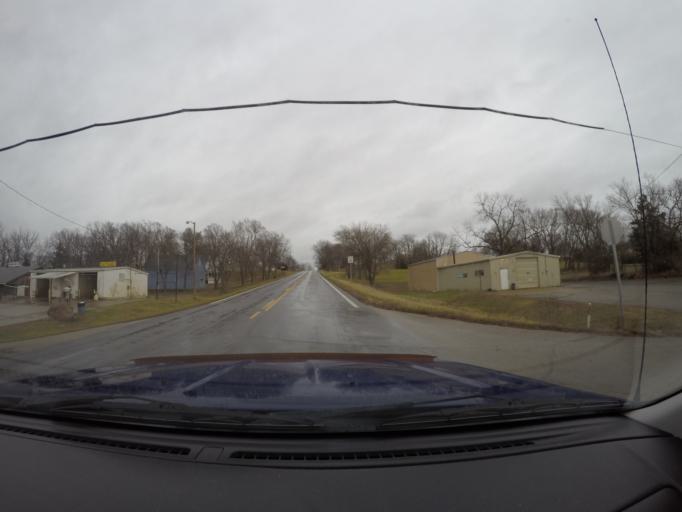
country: US
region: Kansas
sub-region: Jefferson County
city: Valley Falls
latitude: 39.3409
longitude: -95.4655
